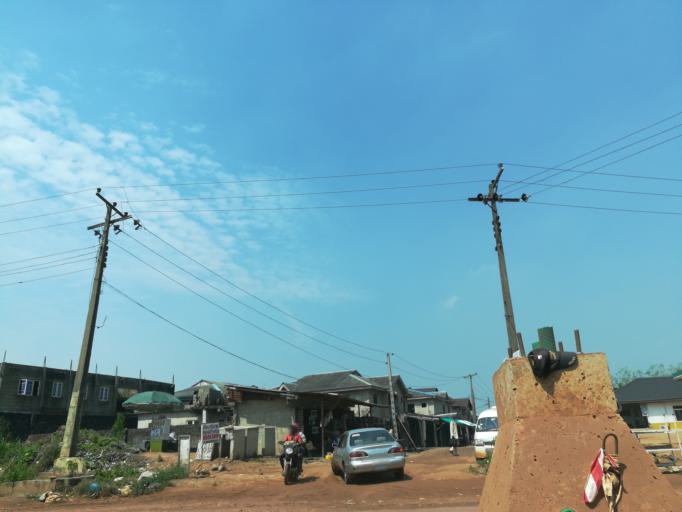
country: NG
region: Lagos
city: Ikorodu
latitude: 6.6565
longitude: 3.4761
